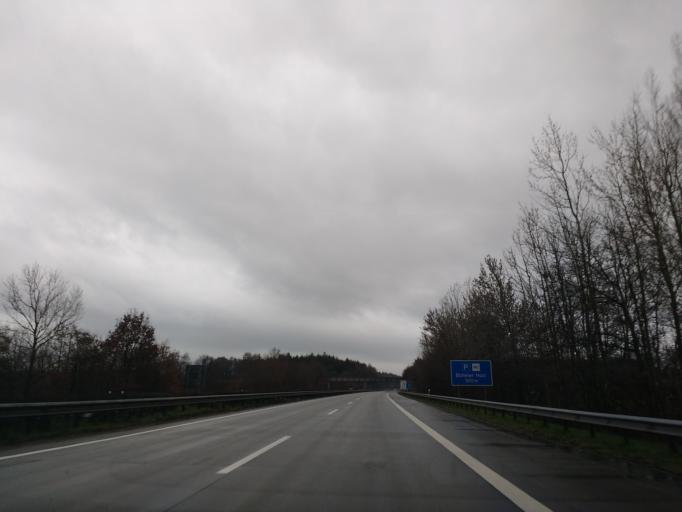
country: DE
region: Lower Saxony
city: Langen
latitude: 53.6175
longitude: 8.6634
